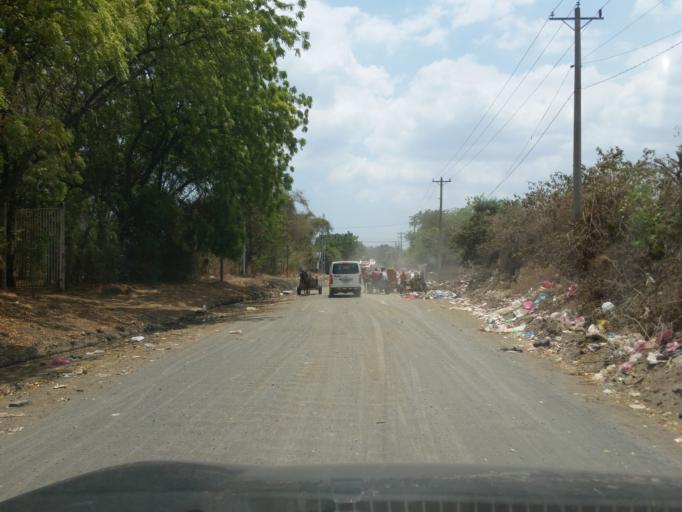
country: NI
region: Managua
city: Managua
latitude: 12.1240
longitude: -86.1655
